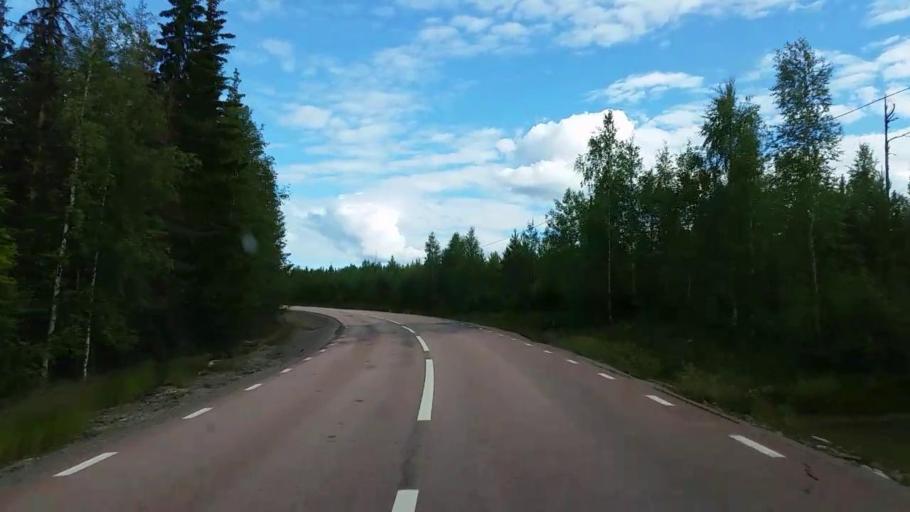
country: SE
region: Gaevleborg
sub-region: Ljusdals Kommun
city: Farila
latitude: 61.9929
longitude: 15.8455
